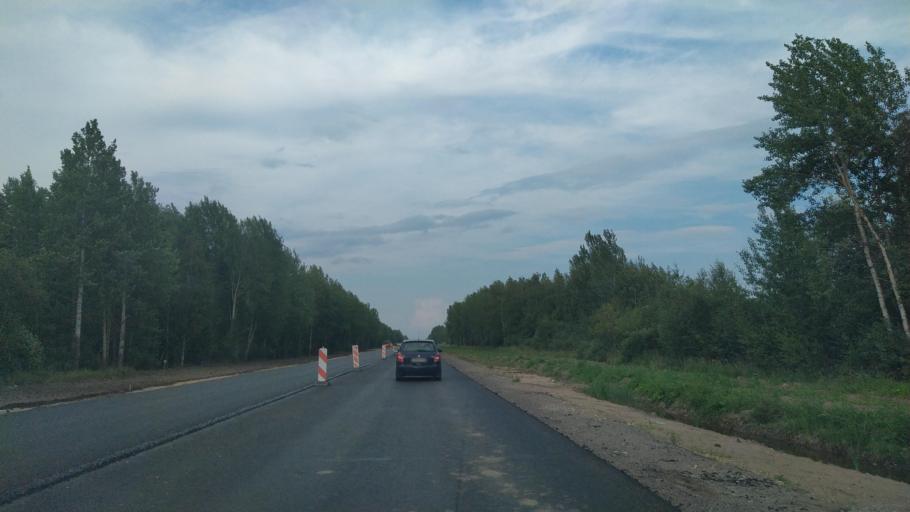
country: RU
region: Novgorod
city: Pankovka
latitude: 58.4048
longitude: 31.0546
